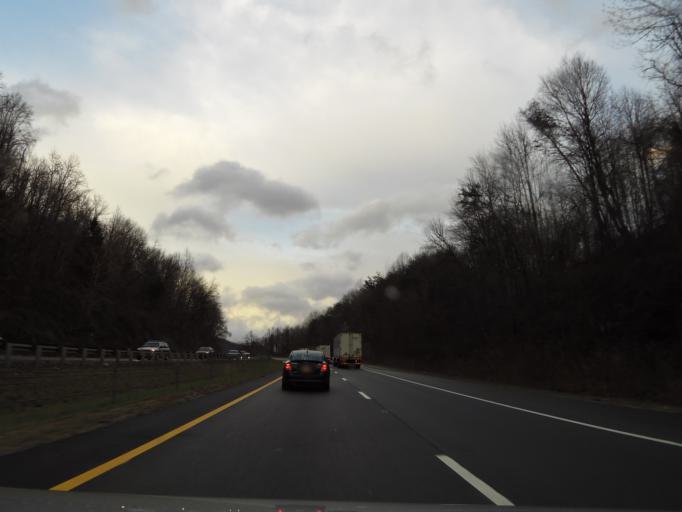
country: US
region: Tennessee
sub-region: Campbell County
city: Caryville
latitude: 36.3175
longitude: -84.2285
